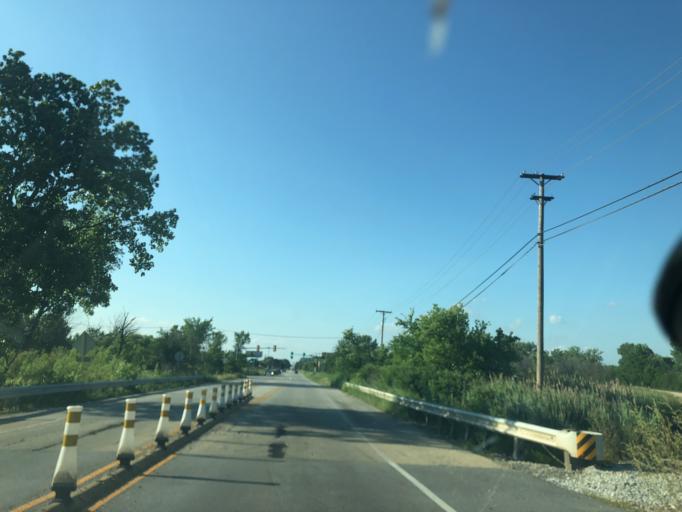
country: US
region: Illinois
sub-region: Will County
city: Mokena
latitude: 41.5719
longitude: -87.8906
